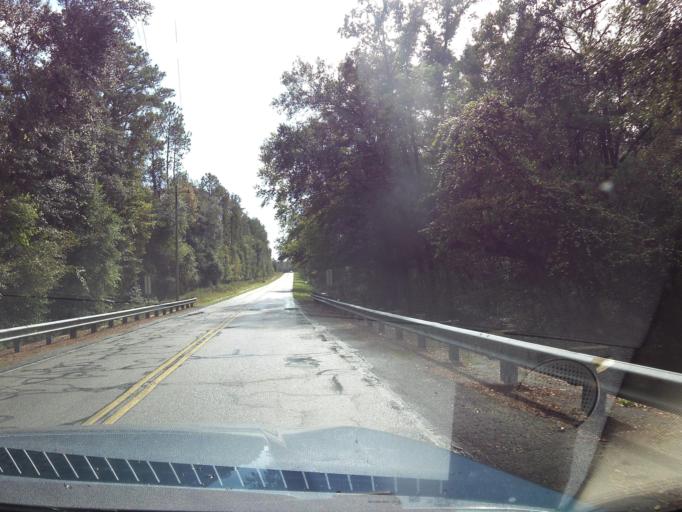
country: US
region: Florida
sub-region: Clay County
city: Asbury Lake
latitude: 30.0019
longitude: -81.8423
